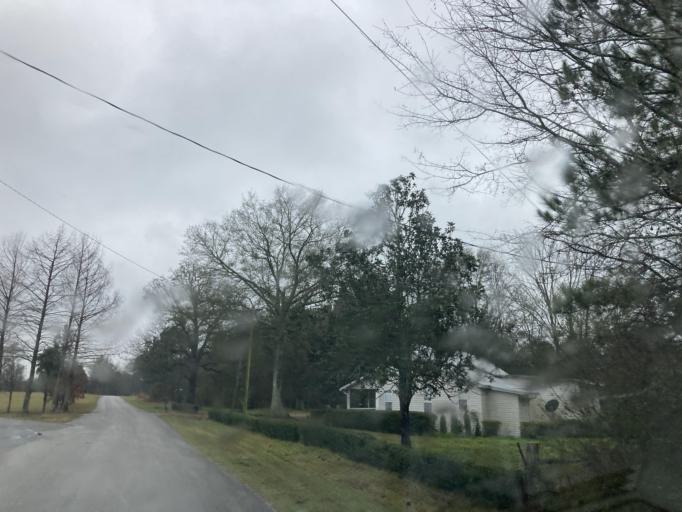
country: US
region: Mississippi
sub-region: Forrest County
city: Rawls Springs
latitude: 31.4876
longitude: -89.3823
